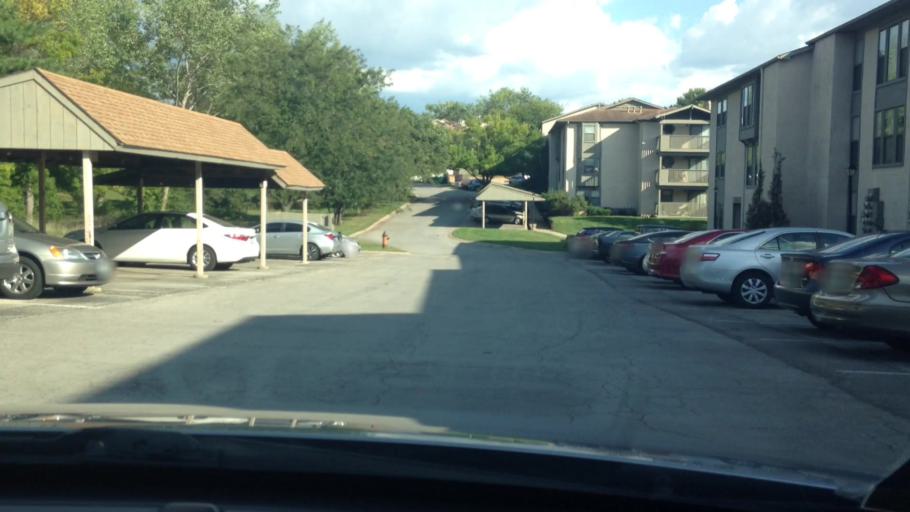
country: US
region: Missouri
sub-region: Clay County
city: Gladstone
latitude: 39.1855
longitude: -94.5800
